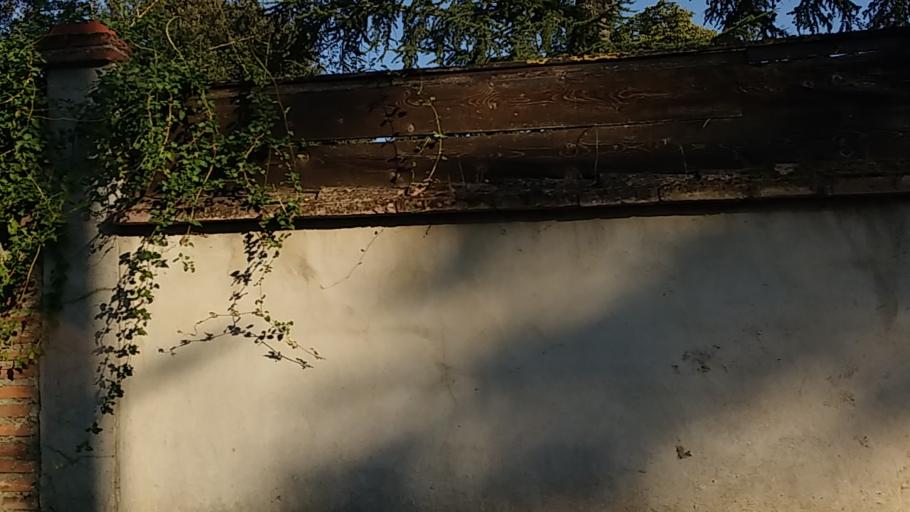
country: FR
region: Midi-Pyrenees
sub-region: Departement de la Haute-Garonne
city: Cugnaux
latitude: 43.5608
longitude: 1.3693
